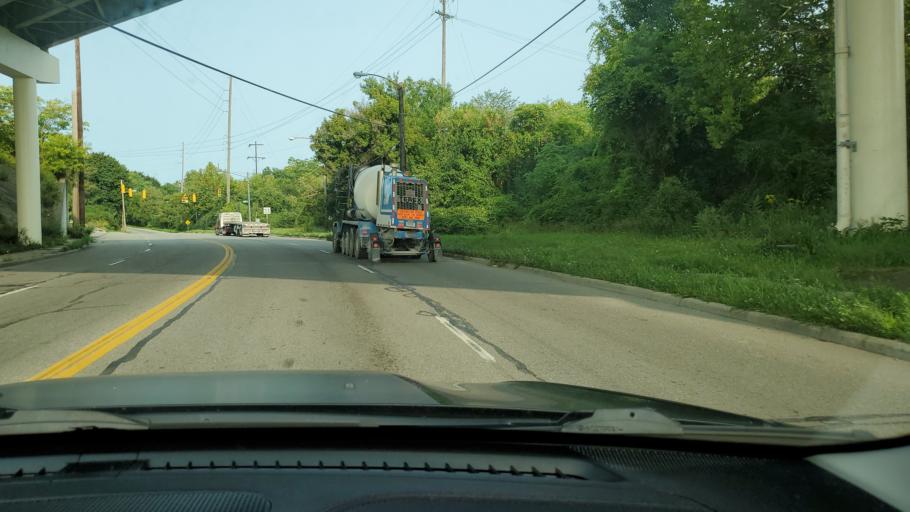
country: US
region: Ohio
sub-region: Mahoning County
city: Youngstown
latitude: 41.0925
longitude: -80.6428
